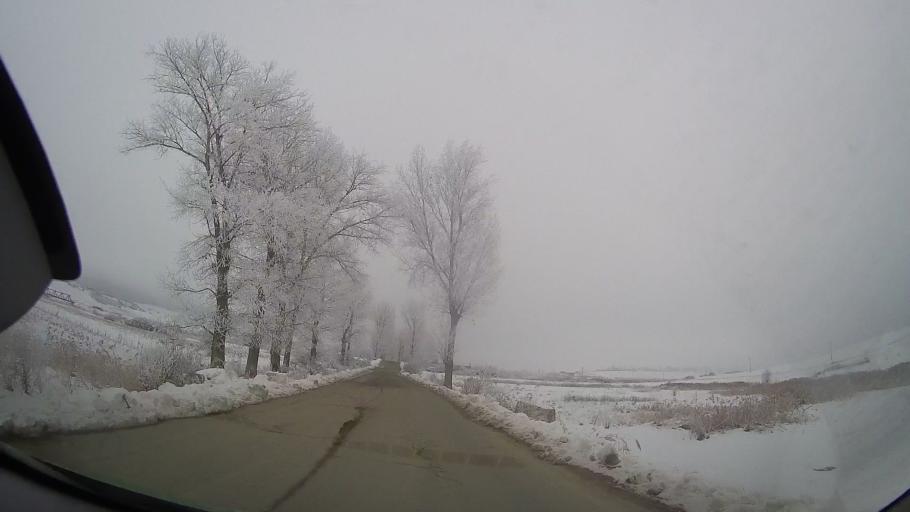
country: RO
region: Iasi
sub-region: Comuna Tansa
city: Tansa
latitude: 46.9124
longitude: 27.2129
